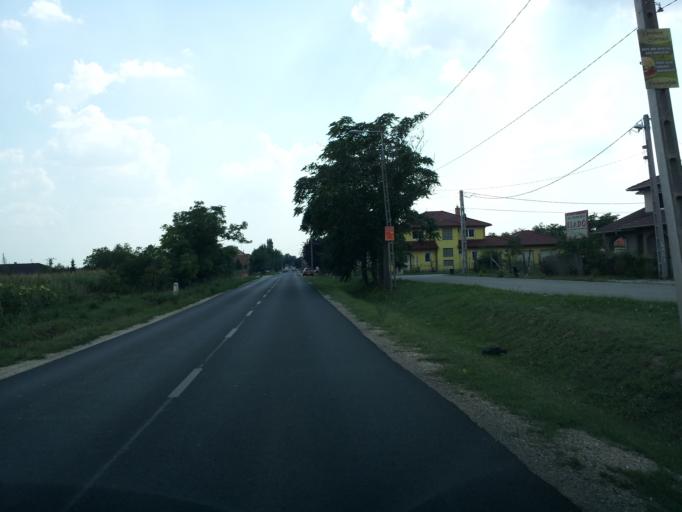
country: HU
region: Pest
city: Toekoel
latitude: 47.3371
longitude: 18.9683
